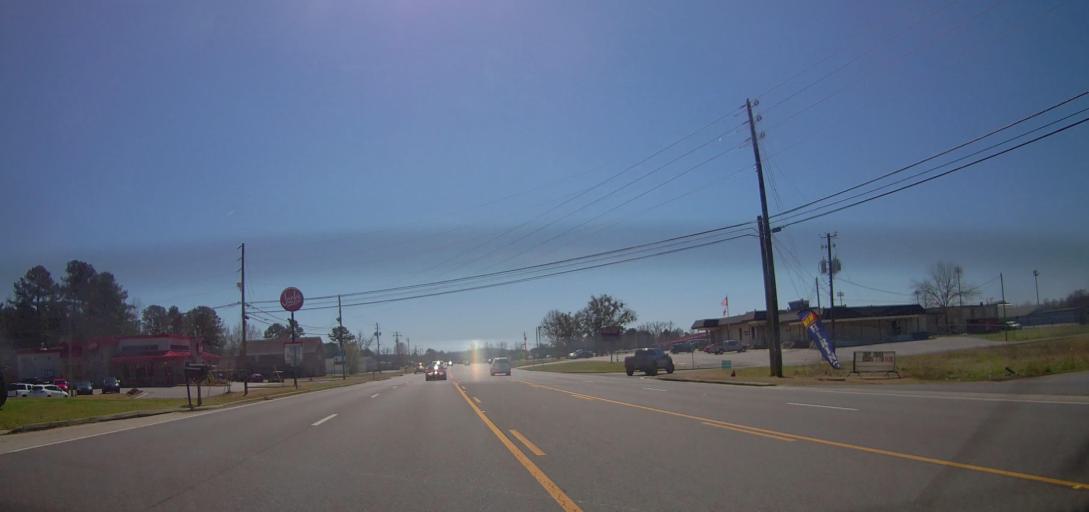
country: US
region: Alabama
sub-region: Etowah County
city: Southside
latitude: 33.9236
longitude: -86.0224
